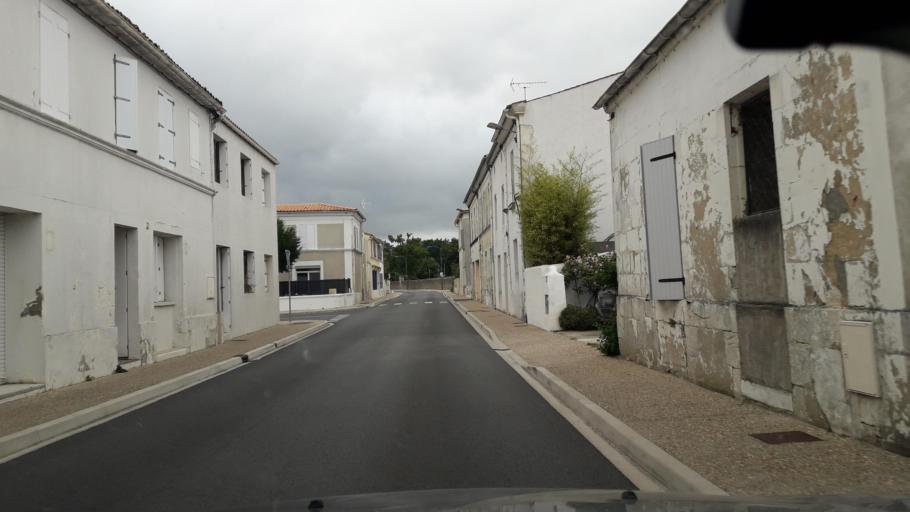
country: FR
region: Poitou-Charentes
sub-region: Departement de la Charente-Maritime
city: Etaules
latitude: 45.7341
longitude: -1.1016
